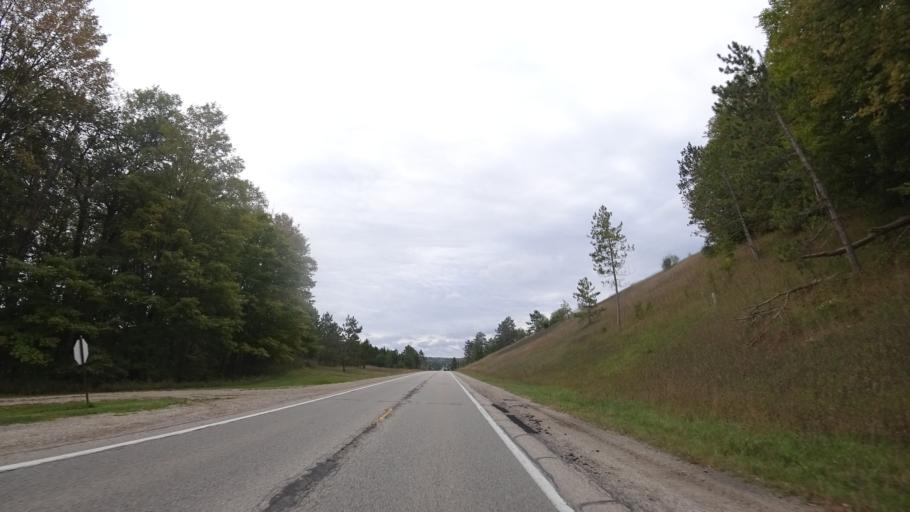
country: US
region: Michigan
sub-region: Charlevoix County
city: Boyne City
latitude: 45.1886
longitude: -84.9150
